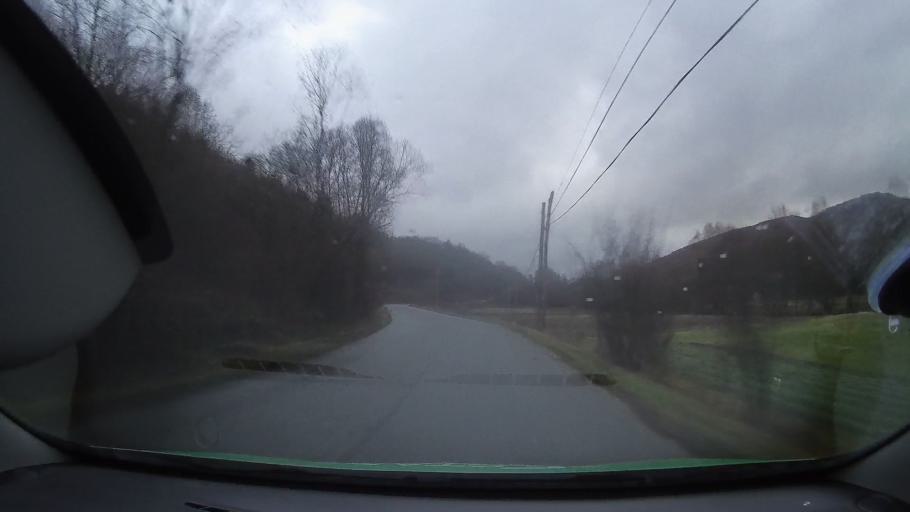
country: RO
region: Hunedoara
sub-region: Comuna Baia de Cris
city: Baia de Cris
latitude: 46.2054
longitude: 22.7166
